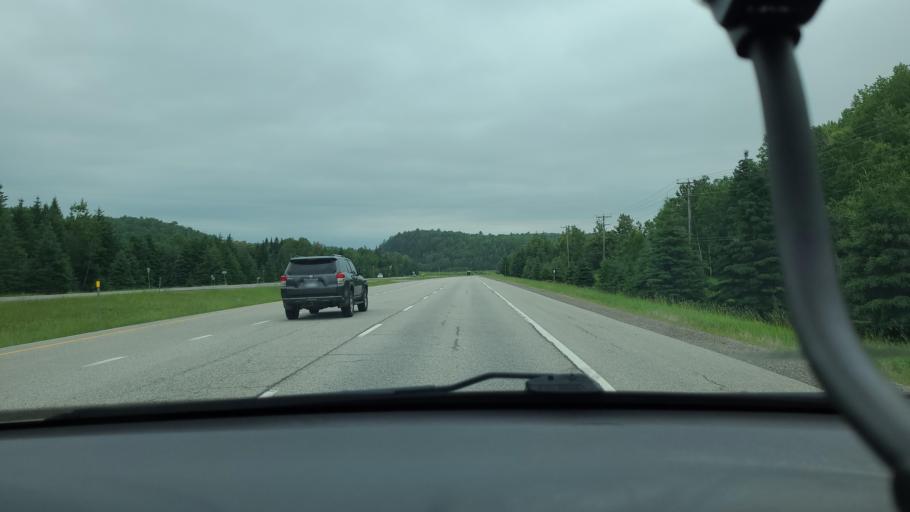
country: CA
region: Quebec
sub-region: Laurentides
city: Labelle
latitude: 46.2246
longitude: -74.7120
